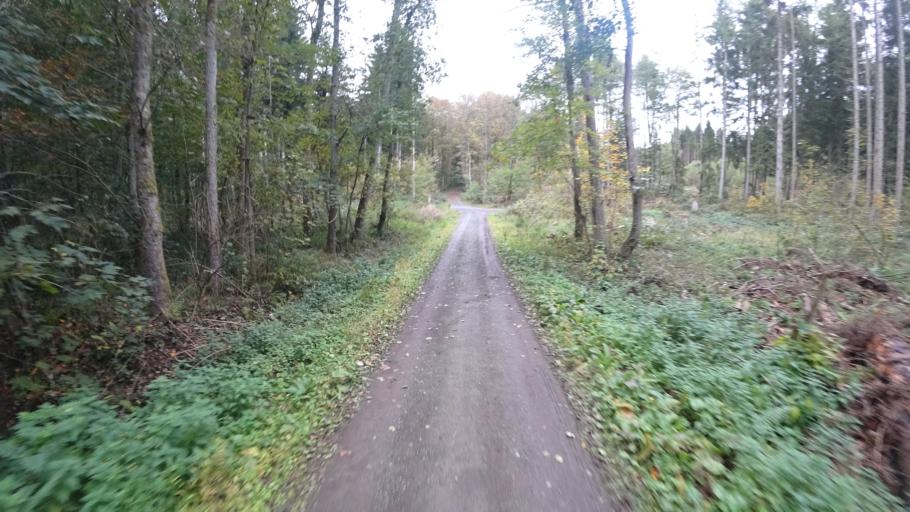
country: DE
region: Rheinland-Pfalz
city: Sessenhausen
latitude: 50.5293
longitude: 7.7322
